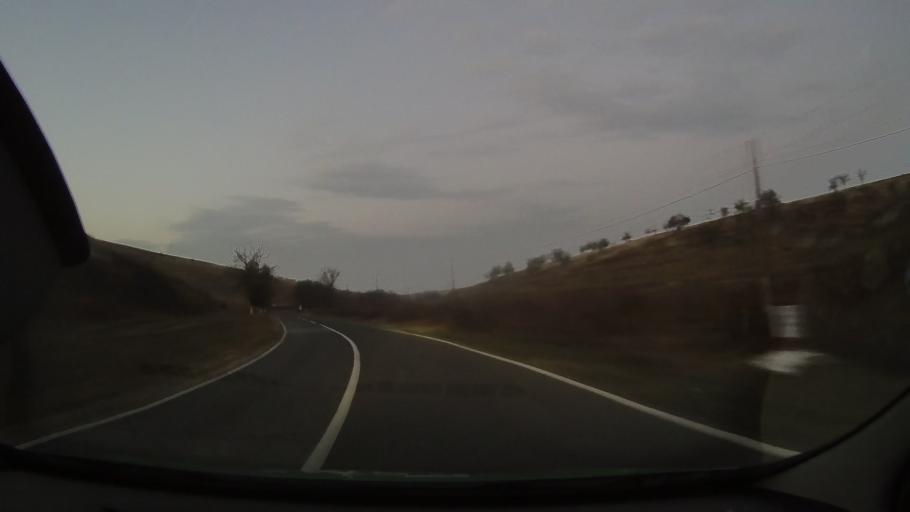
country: RO
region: Constanta
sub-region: Comuna Ion Corvin
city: Ion Corvin
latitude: 44.1012
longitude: 27.7552
